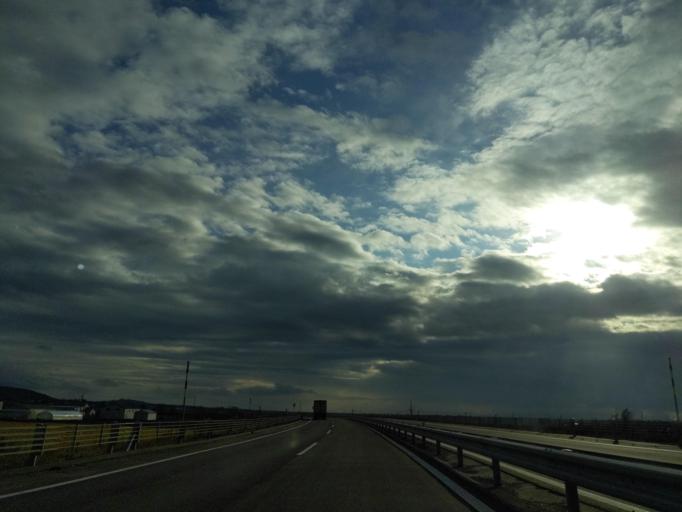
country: JP
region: Hokkaido
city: Chitose
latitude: 42.9484
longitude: 141.7137
